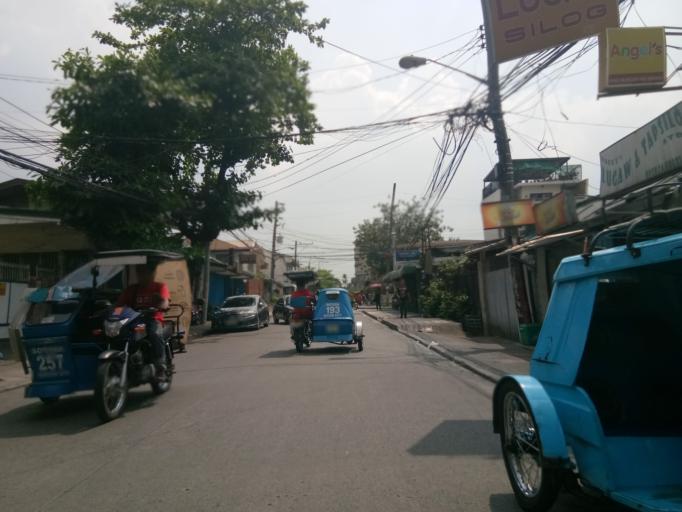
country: PH
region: Metro Manila
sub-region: San Juan
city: San Juan
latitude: 14.6179
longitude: 121.0574
